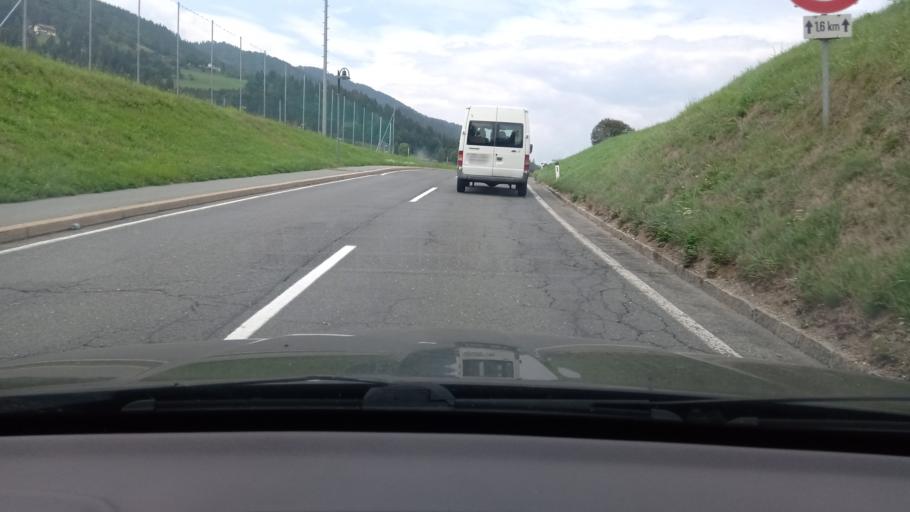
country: AT
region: Carinthia
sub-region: Politischer Bezirk Hermagor
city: Hermagor
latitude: 46.6301
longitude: 13.3590
